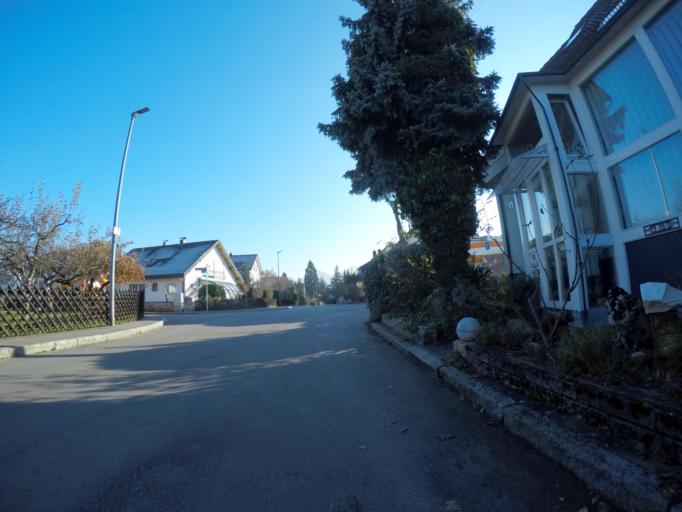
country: DE
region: Baden-Wuerttemberg
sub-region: Tuebingen Region
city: Reutlingen
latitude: 48.5187
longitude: 9.2210
